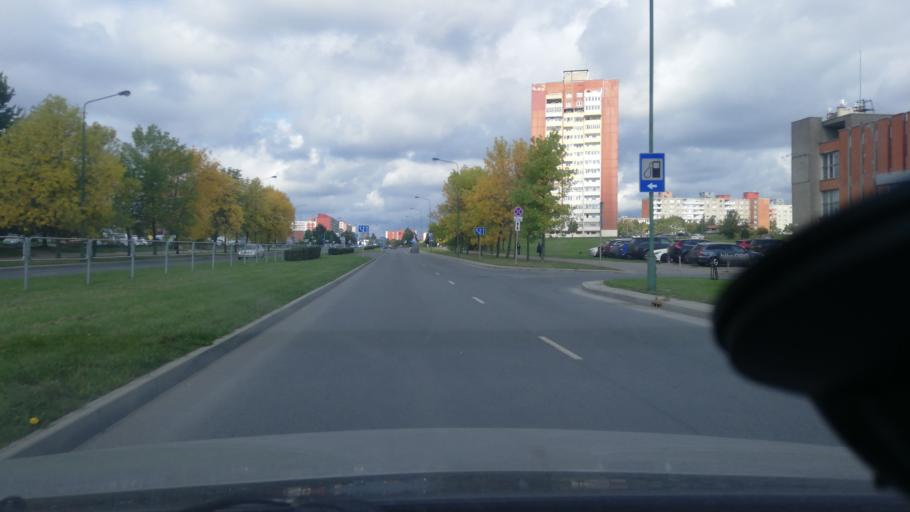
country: LT
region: Klaipedos apskritis
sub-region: Klaipeda
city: Klaipeda
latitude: 55.6680
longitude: 21.1950
